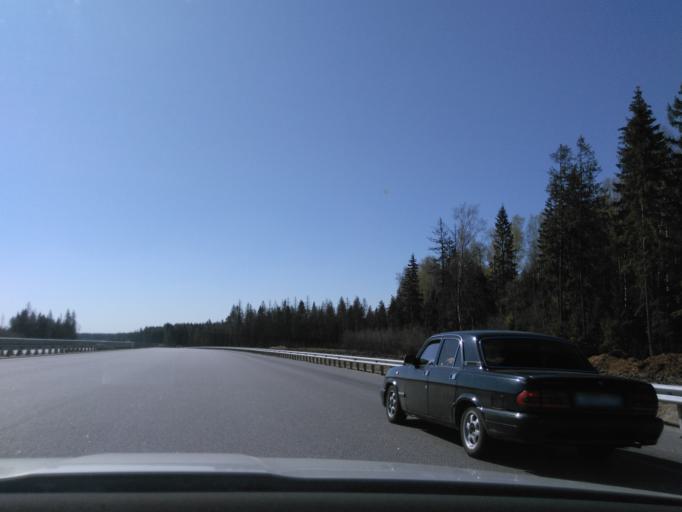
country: RU
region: Moskovskaya
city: Skhodnya
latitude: 55.9873
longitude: 37.3060
